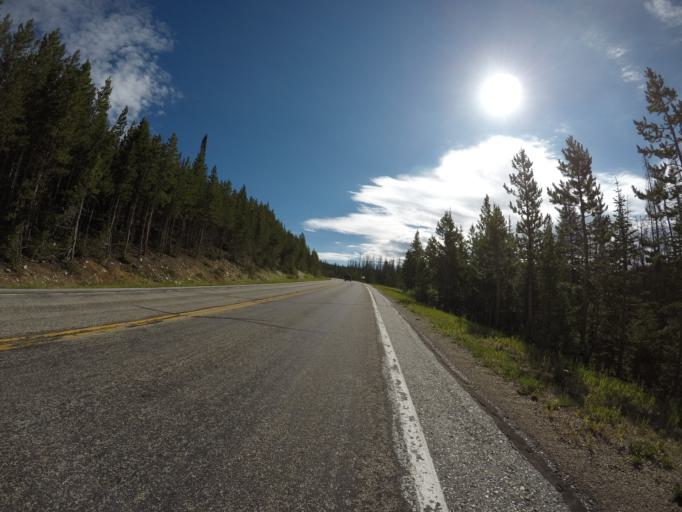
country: US
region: Wyoming
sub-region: Carbon County
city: Saratoga
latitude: 41.3242
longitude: -106.4472
